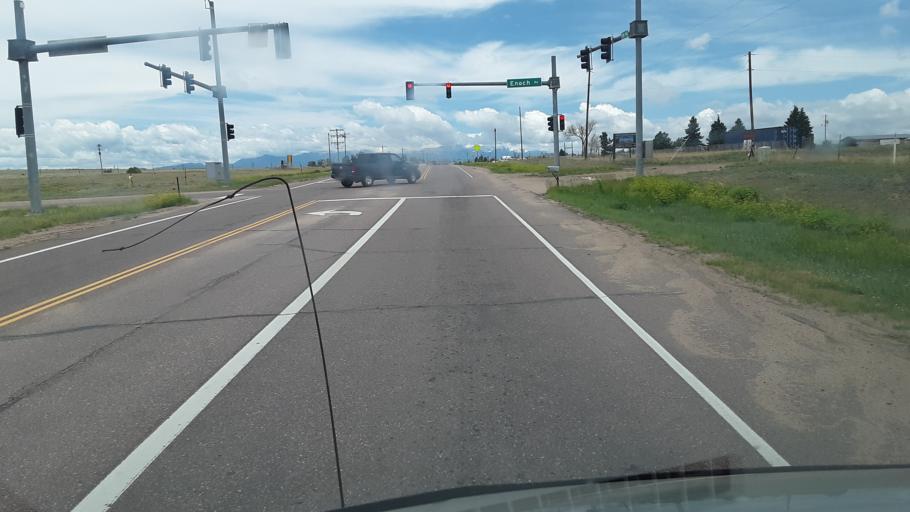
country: US
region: Colorado
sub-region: El Paso County
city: Ellicott
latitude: 38.8387
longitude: -104.5344
